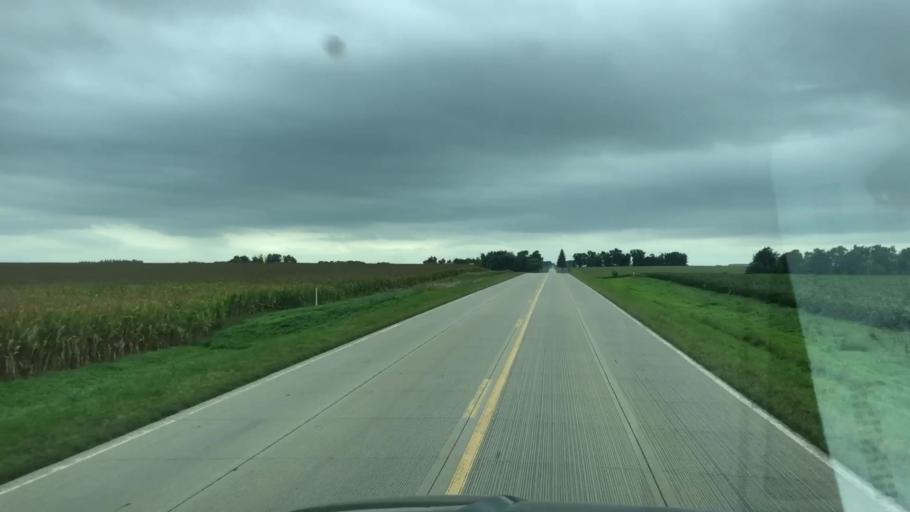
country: US
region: Iowa
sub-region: Sioux County
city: Alton
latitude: 43.1173
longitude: -95.9788
